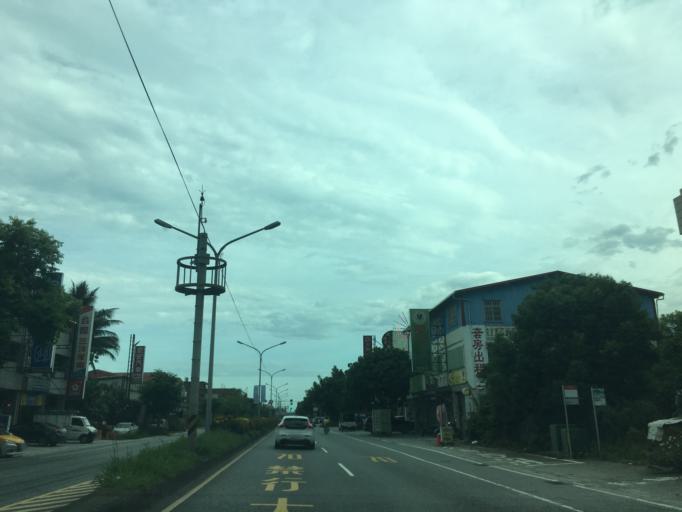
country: TW
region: Taiwan
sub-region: Hualien
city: Hualian
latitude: 24.0365
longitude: 121.6048
